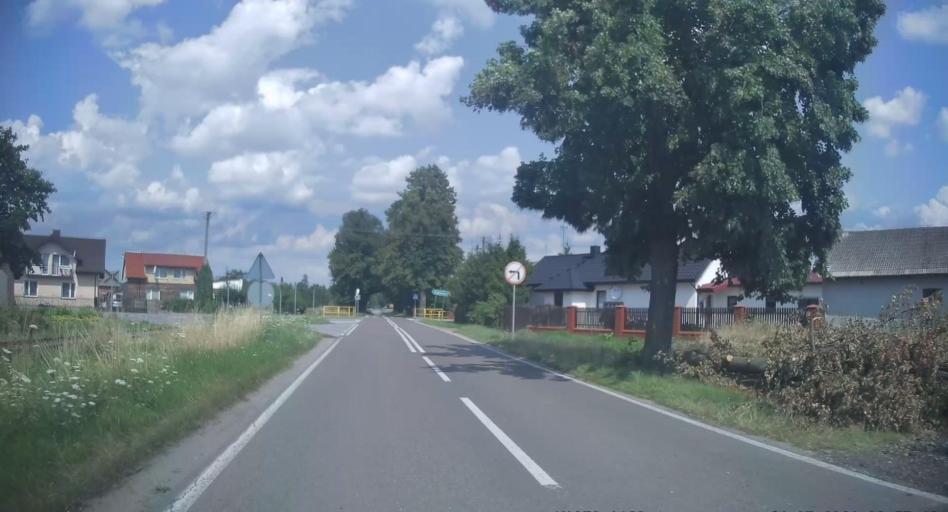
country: PL
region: Lodz Voivodeship
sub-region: Powiat tomaszowski
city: Lubochnia
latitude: 51.5726
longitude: 20.0974
